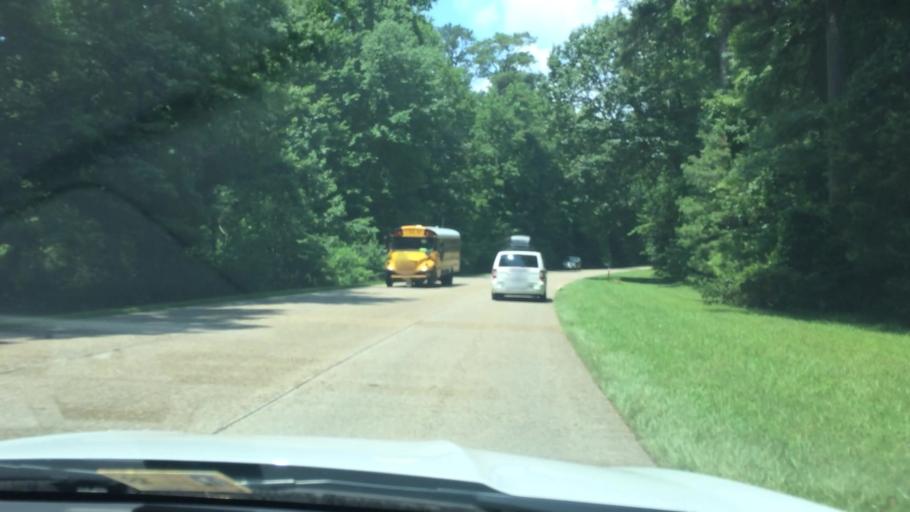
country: US
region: Virginia
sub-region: York County
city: Yorktown
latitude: 37.2308
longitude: -76.5205
